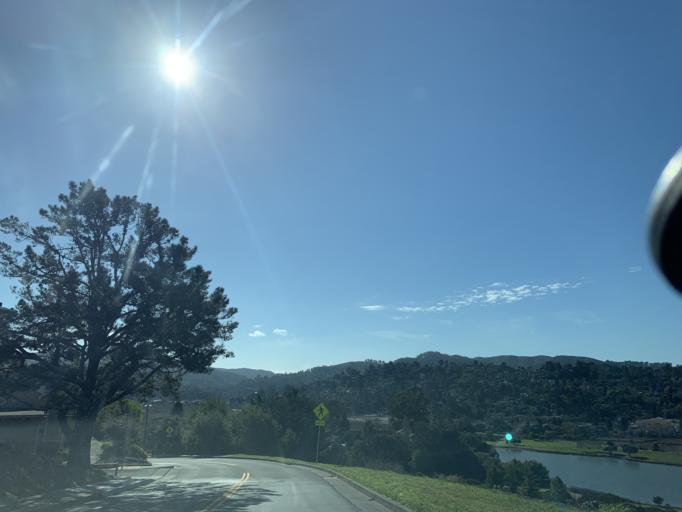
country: US
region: California
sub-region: Marin County
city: Strawberry
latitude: 37.8963
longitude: -122.5201
